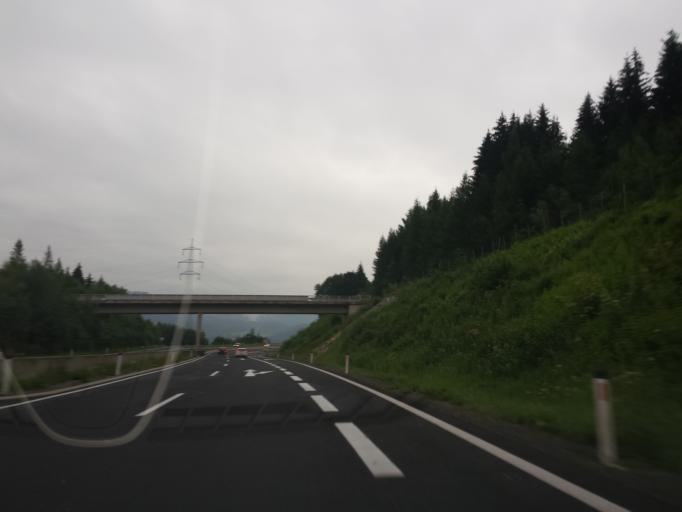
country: AT
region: Styria
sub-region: Politischer Bezirk Bruck-Muerzzuschlag
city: Mitterdorf im Muerztal
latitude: 47.5292
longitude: 15.5205
